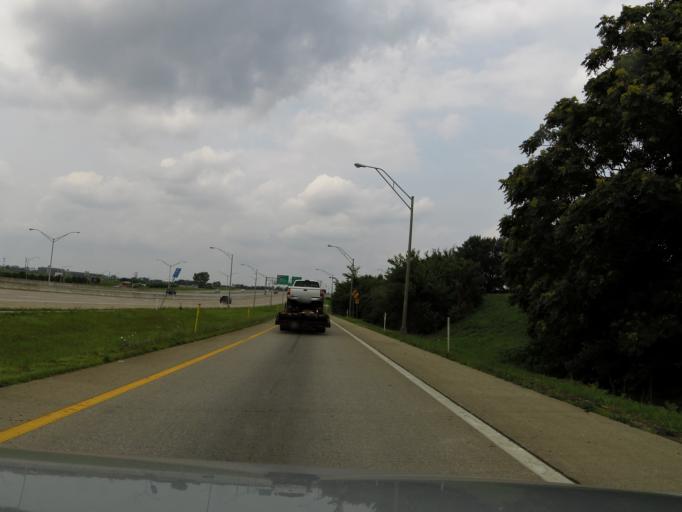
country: US
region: Kentucky
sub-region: Jefferson County
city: Audubon Park
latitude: 38.1862
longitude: -85.7249
